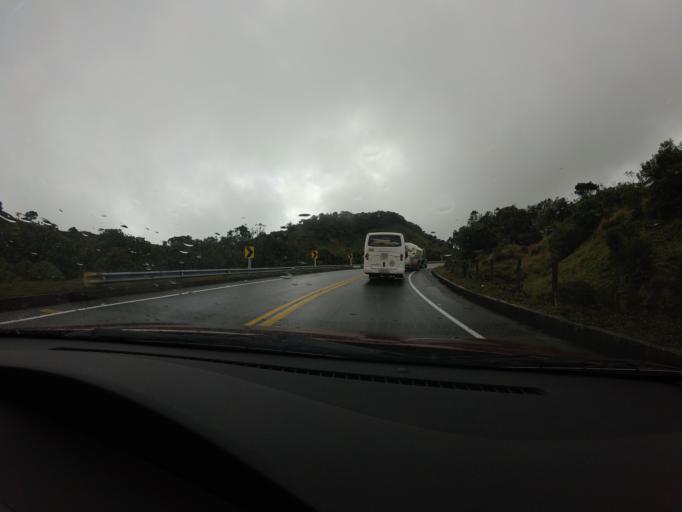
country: CO
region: Tolima
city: Herveo
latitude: 5.0714
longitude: -75.2861
